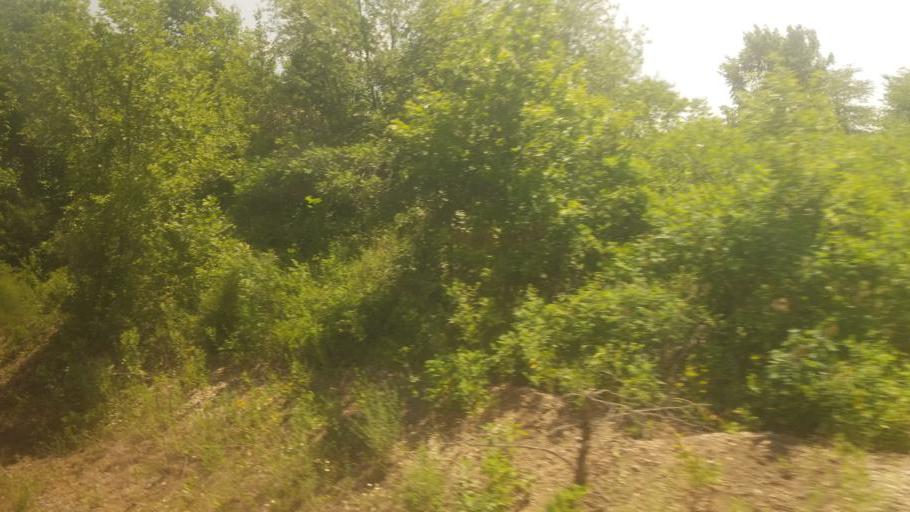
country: US
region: Missouri
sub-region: Linn County
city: Marceline
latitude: 39.8626
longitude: -92.8016
